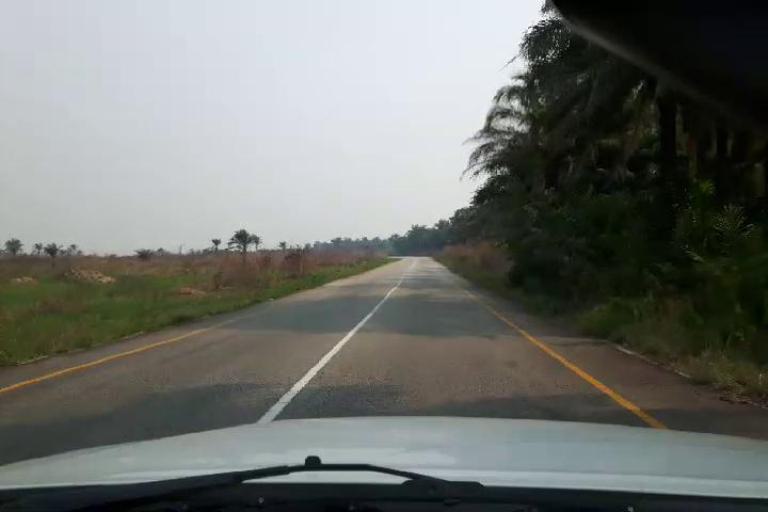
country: SL
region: Southern Province
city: Largo
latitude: 8.2163
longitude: -12.0743
